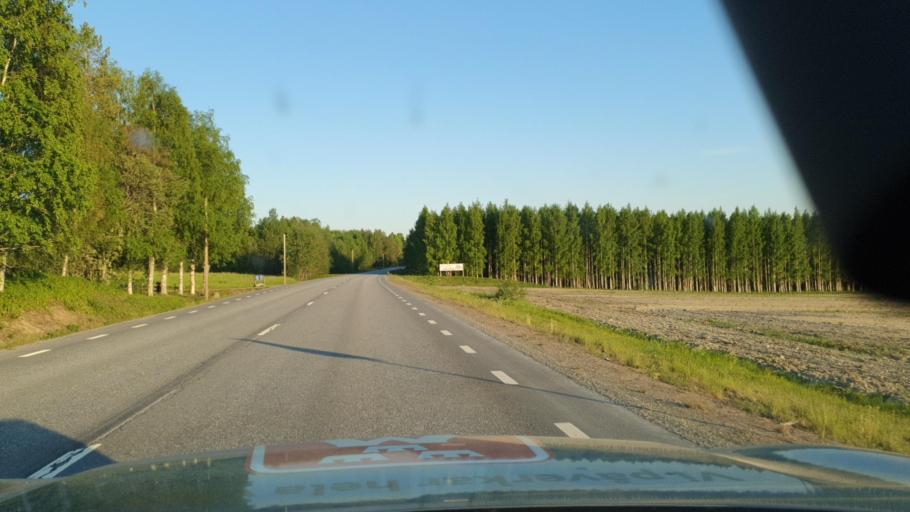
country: SE
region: Vaesternorrland
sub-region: Solleftea Kommun
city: Solleftea
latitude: 63.2246
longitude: 17.2197
